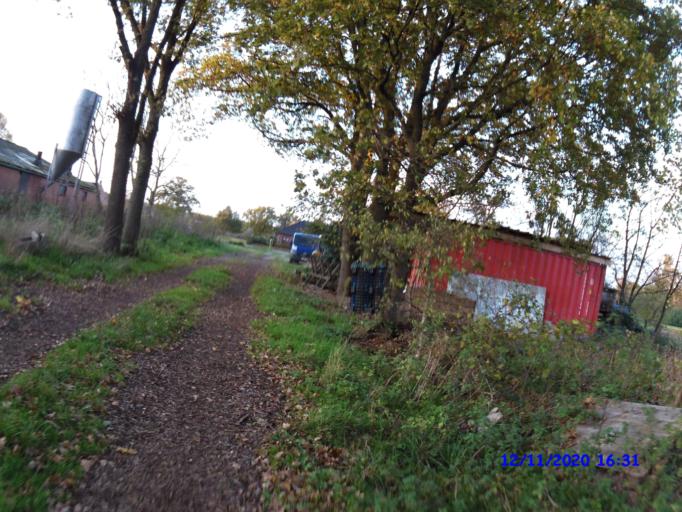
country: BE
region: Flanders
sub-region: Provincie Antwerpen
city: Meerhout
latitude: 51.1866
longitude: 5.0524
